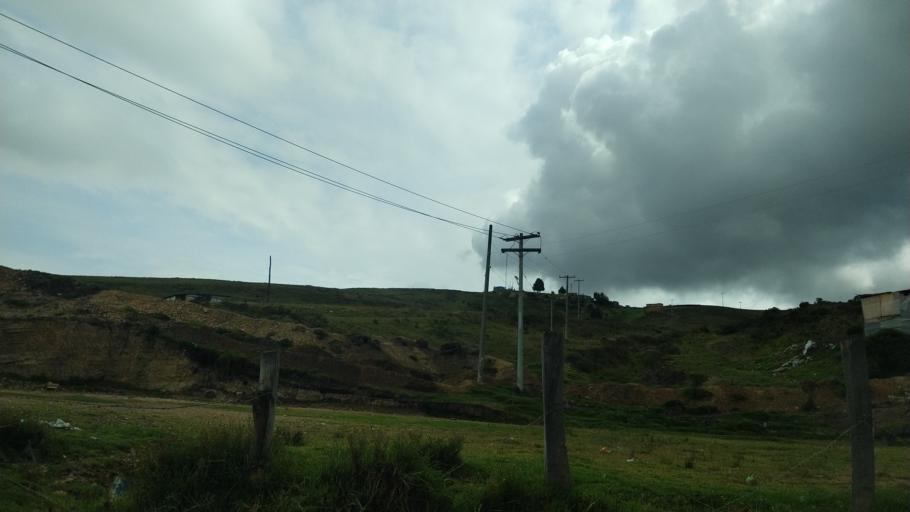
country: CO
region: Cundinamarca
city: Soacha
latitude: 4.5622
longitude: -74.1865
